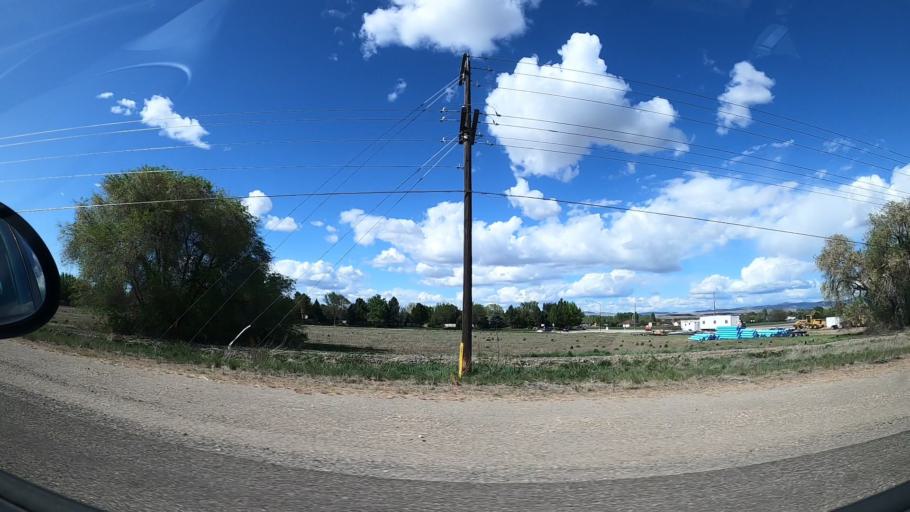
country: US
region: Idaho
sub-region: Ada County
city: Eagle
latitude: 43.6955
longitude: -116.3794
